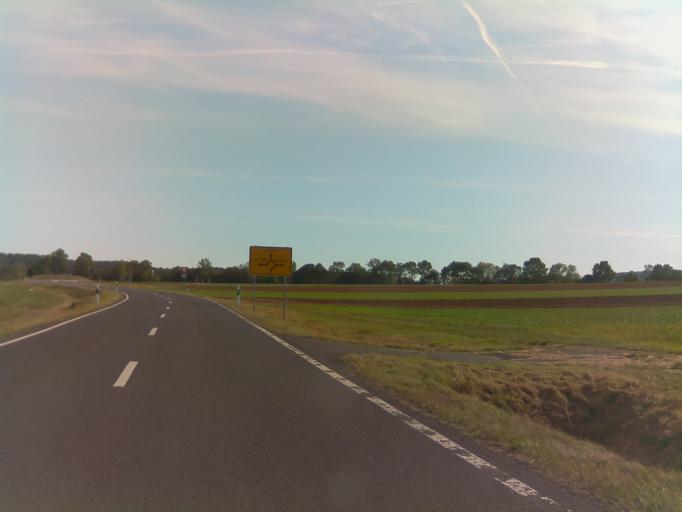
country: DE
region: Bavaria
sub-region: Regierungsbezirk Unterfranken
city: Fladungen
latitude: 50.5103
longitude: 10.1489
